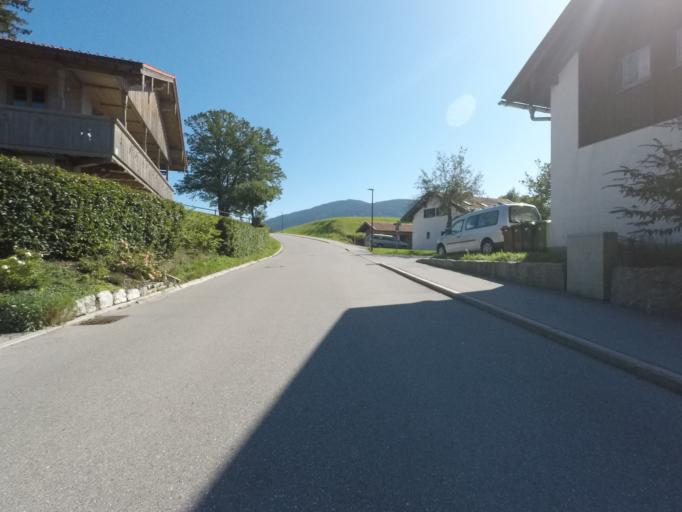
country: DE
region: Bavaria
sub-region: Upper Bavaria
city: Gaissach
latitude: 47.7397
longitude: 11.5715
